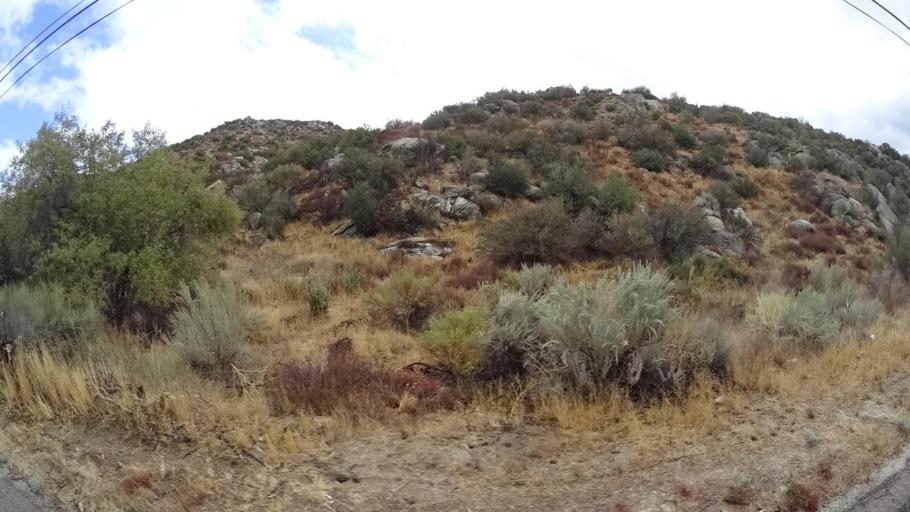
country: US
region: California
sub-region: San Diego County
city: Campo
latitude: 32.7019
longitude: -116.4324
